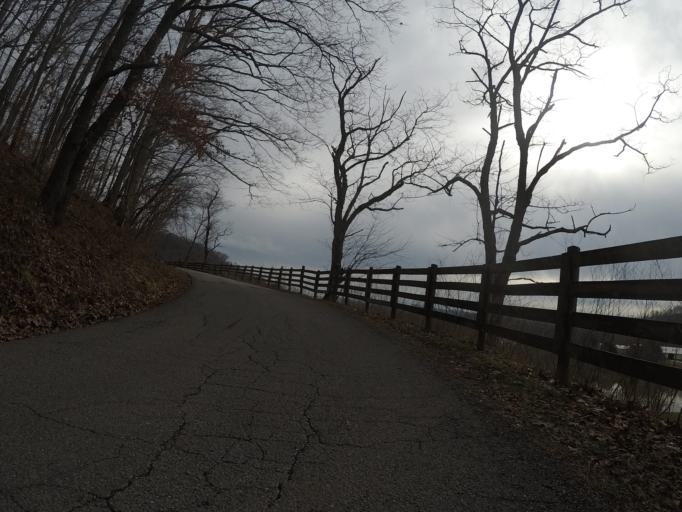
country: US
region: West Virginia
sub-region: Cabell County
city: Huntington
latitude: 38.4388
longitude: -82.4617
